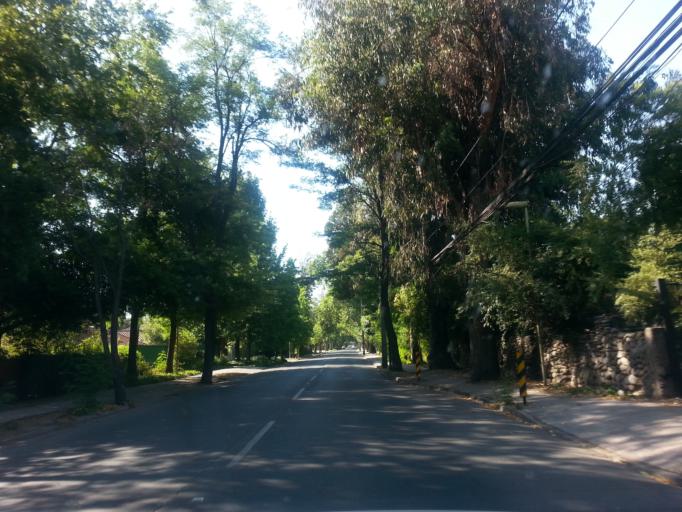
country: CL
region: Santiago Metropolitan
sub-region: Provincia de Santiago
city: Villa Presidente Frei, Nunoa, Santiago, Chile
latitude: -33.3752
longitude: -70.5092
